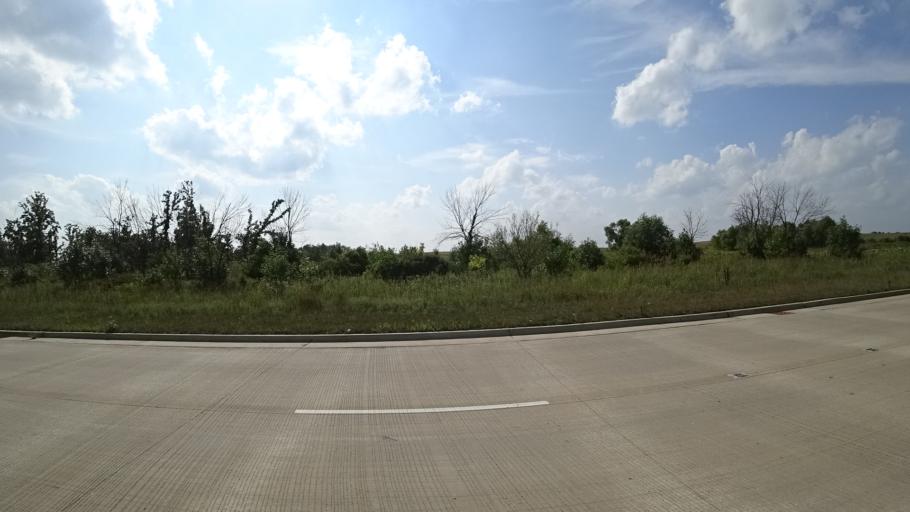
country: US
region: Illinois
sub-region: Cook County
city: Orland Hills
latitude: 41.5686
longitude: -87.8516
